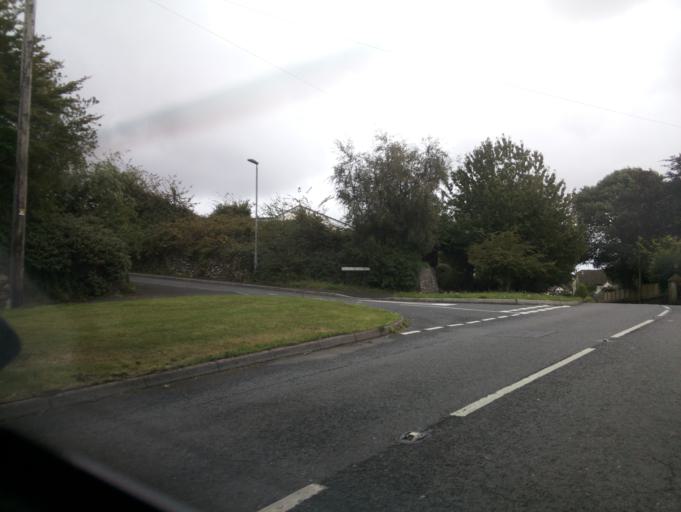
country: GB
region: England
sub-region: Devon
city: Kingsbridge
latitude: 50.2731
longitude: -3.7041
